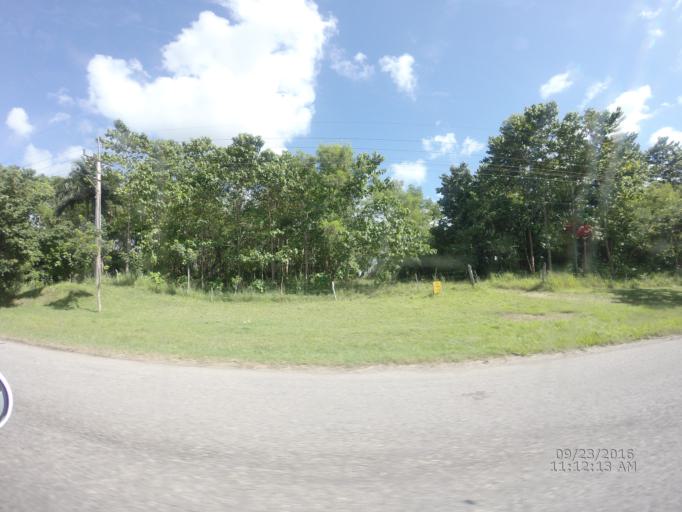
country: CU
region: La Habana
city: Arroyo Naranjo
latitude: 23.0285
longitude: -82.2805
